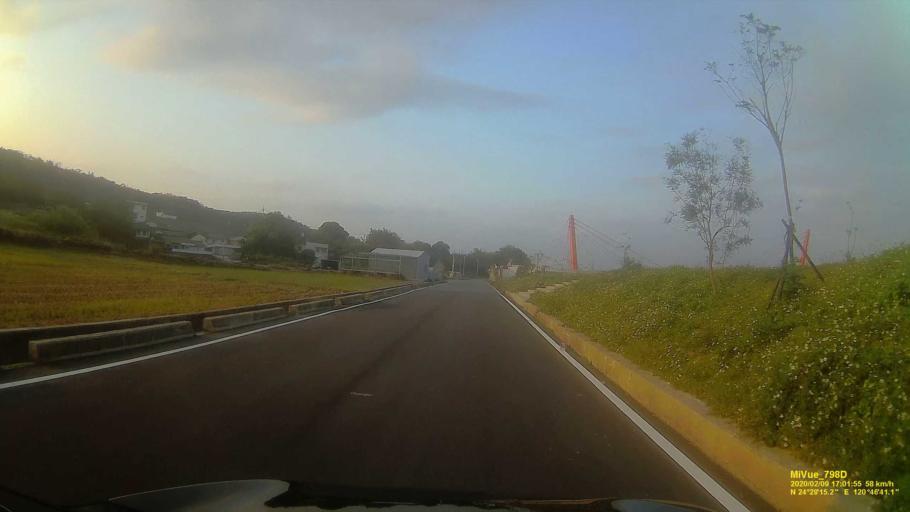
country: TW
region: Taiwan
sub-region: Miaoli
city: Miaoli
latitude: 24.4878
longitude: 120.7779
